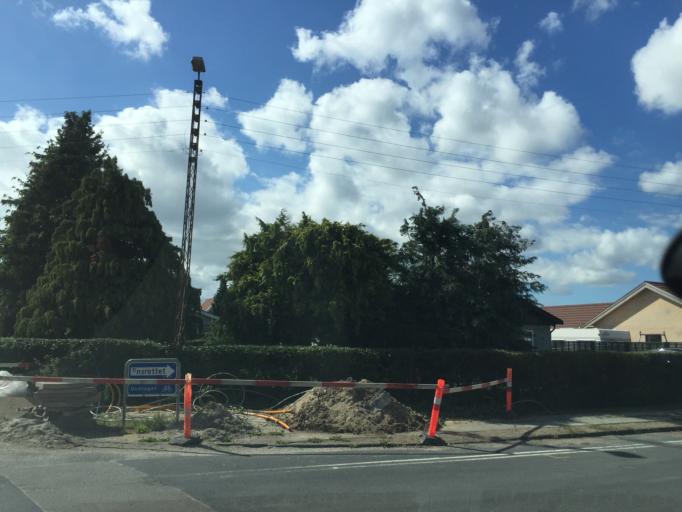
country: DK
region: South Denmark
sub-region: Odense Kommune
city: Odense
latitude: 55.3599
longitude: 10.3984
